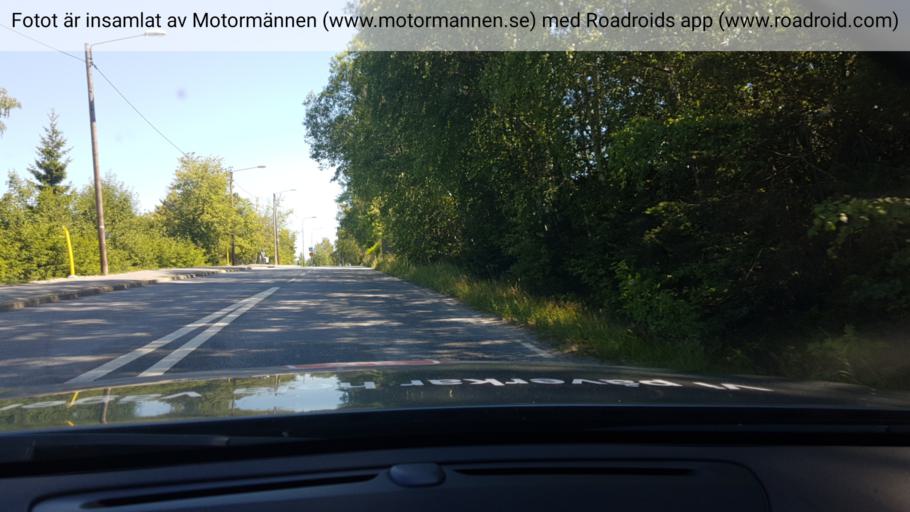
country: SE
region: Stockholm
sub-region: Haninge Kommun
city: Haninge
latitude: 59.1911
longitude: 18.1826
